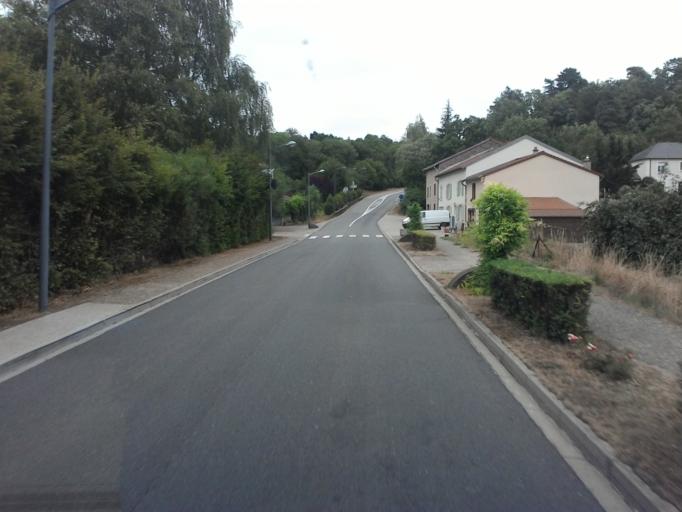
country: FR
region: Lorraine
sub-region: Departement de Meurthe-et-Moselle
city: Colombey-les-Belles
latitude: 48.5739
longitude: 5.9739
